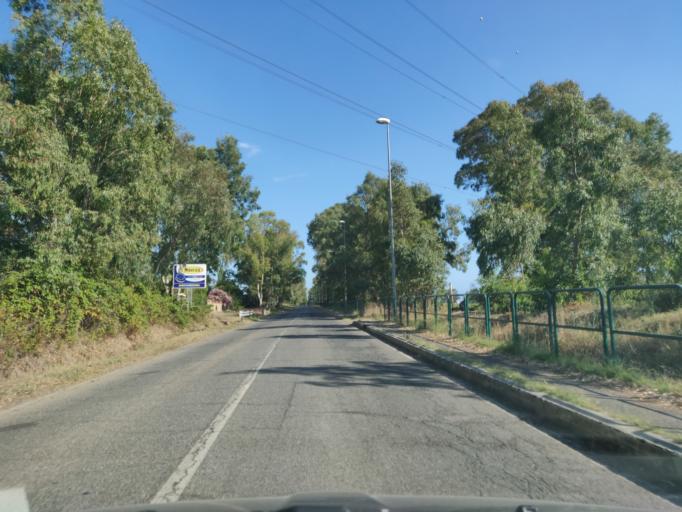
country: IT
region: Latium
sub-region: Citta metropolitana di Roma Capitale
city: Aurelia
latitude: 42.1385
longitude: 11.7675
